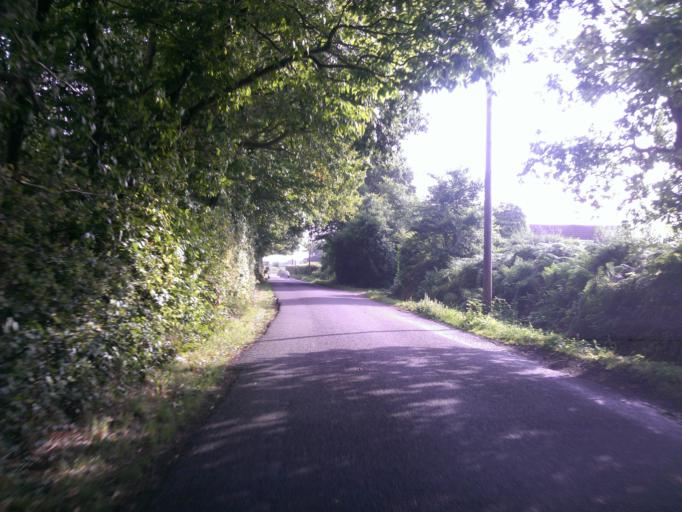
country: GB
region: England
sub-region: Essex
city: Little Clacton
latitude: 51.8405
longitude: 1.1047
